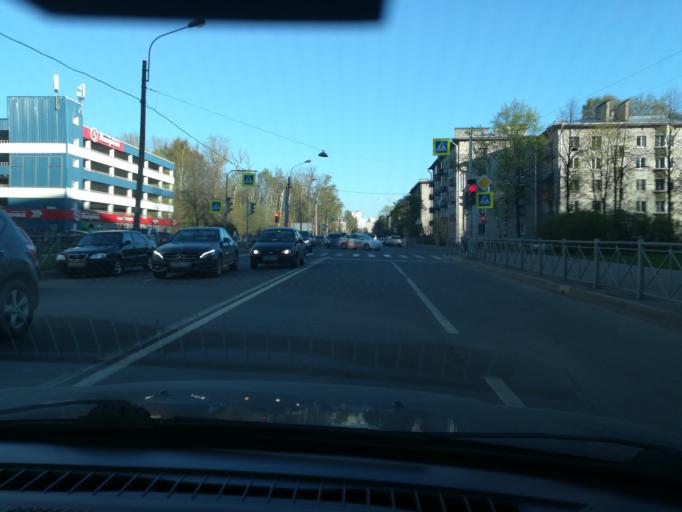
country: RU
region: St.-Petersburg
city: Vasyl'evsky Ostrov
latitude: 59.9448
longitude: 30.2372
